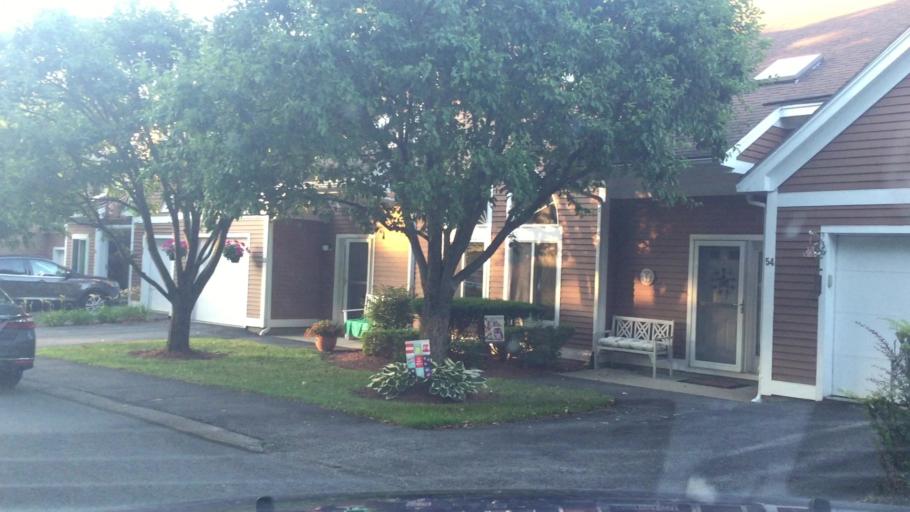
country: US
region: Massachusetts
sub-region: Essex County
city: Haverhill
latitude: 42.8035
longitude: -71.0769
